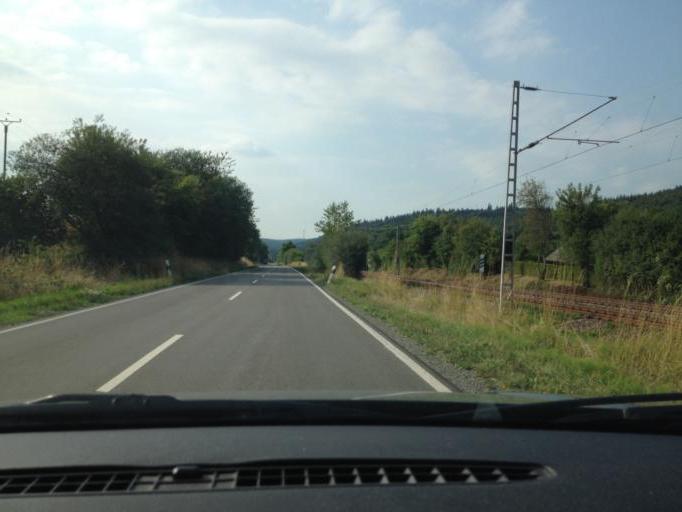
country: DE
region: Saarland
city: Nohfelden
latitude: 49.5642
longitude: 7.1247
